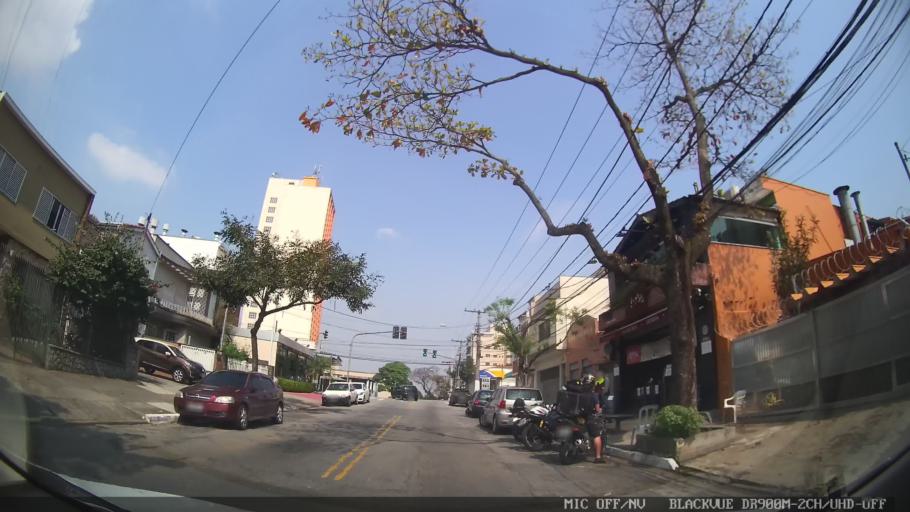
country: BR
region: Sao Paulo
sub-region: Sao Paulo
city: Sao Paulo
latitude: -23.5778
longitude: -46.6214
